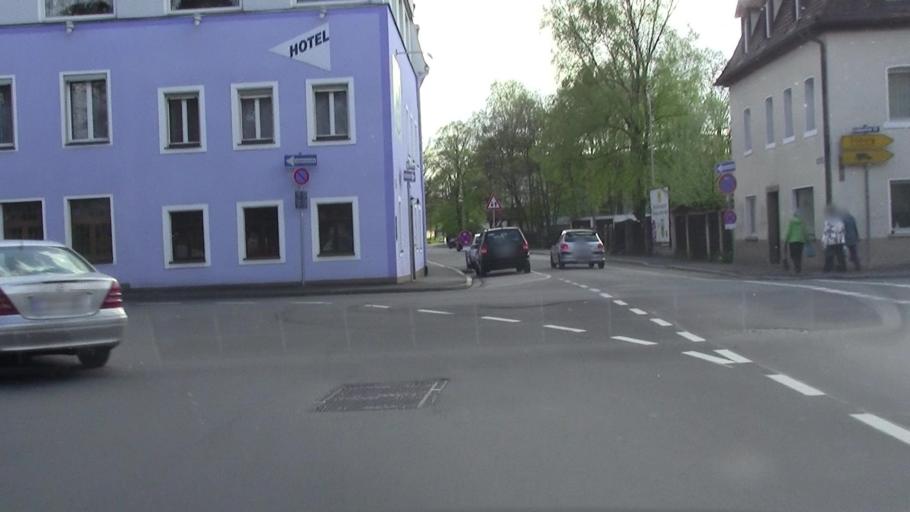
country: DE
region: Bavaria
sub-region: Upper Franconia
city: Kulmbach
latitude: 50.1058
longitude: 11.4483
